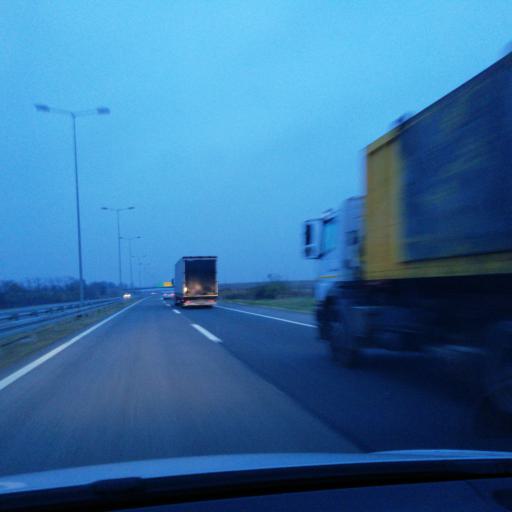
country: RS
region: Autonomna Pokrajina Vojvodina
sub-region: Sremski Okrug
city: Ruma
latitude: 44.9648
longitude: 19.8002
